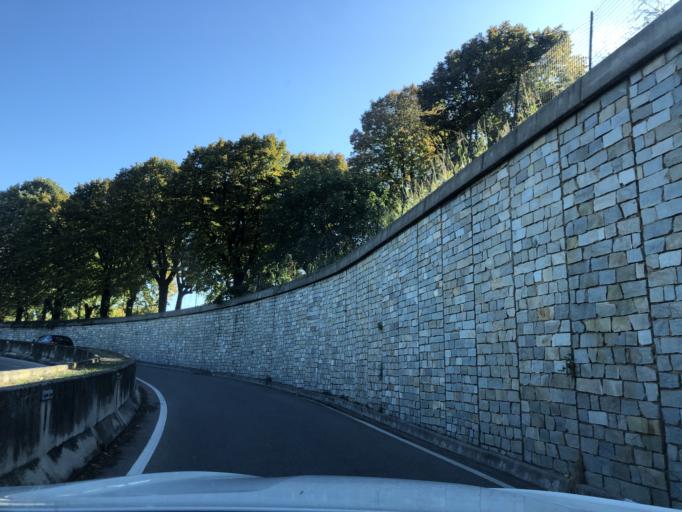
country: IT
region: Lombardy
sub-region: Provincia di Monza e Brianza
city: Limbiate
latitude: 45.6056
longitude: 9.1312
